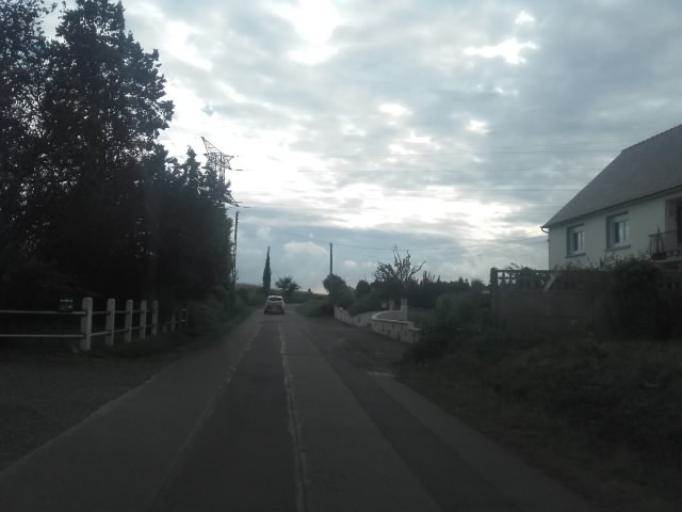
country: FR
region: Brittany
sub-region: Departement des Cotes-d'Armor
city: Pordic
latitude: 48.5635
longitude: -2.8304
